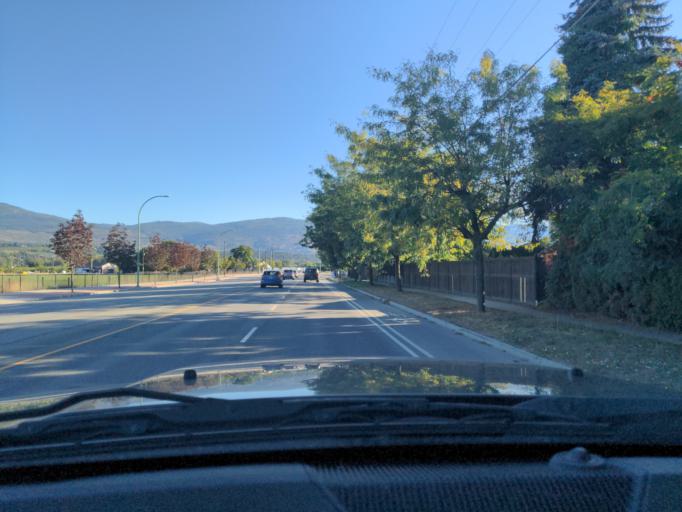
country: CA
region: British Columbia
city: Kelowna
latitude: 49.8557
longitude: -119.4745
